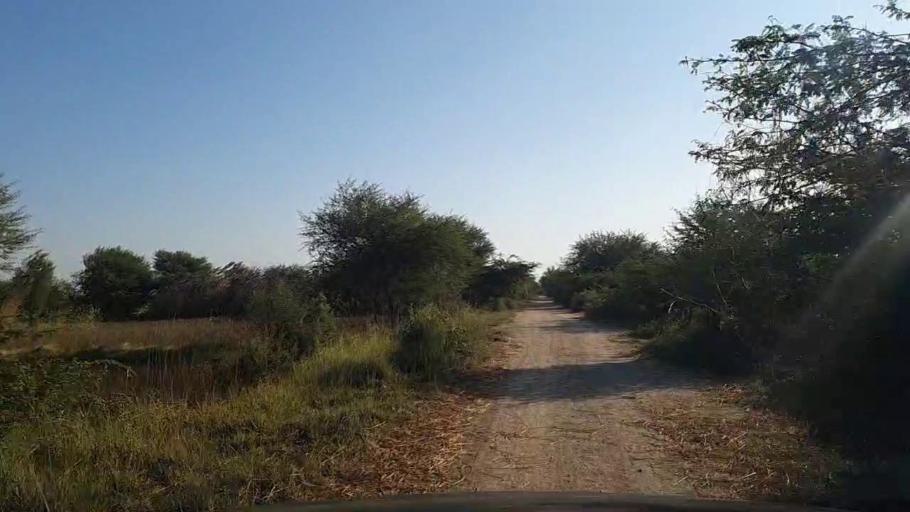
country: PK
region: Sindh
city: Mirpur Batoro
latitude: 24.6749
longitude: 68.3644
